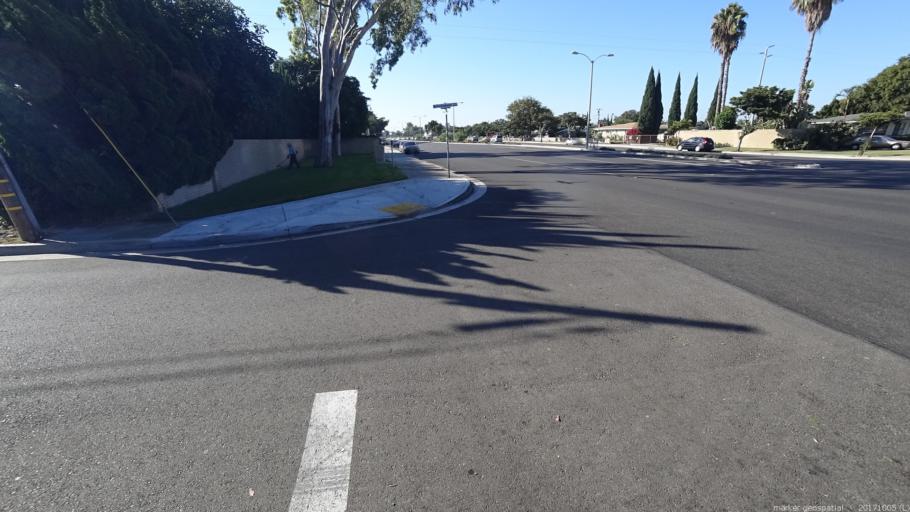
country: US
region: California
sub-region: Orange County
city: Garden Grove
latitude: 33.7982
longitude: -117.9585
